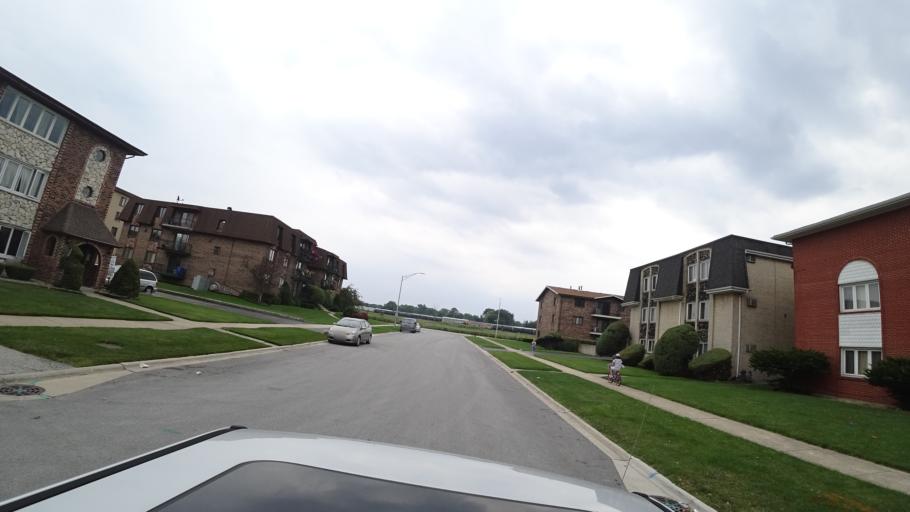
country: US
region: Illinois
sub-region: Cook County
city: Oak Lawn
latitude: 41.7023
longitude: -87.7658
